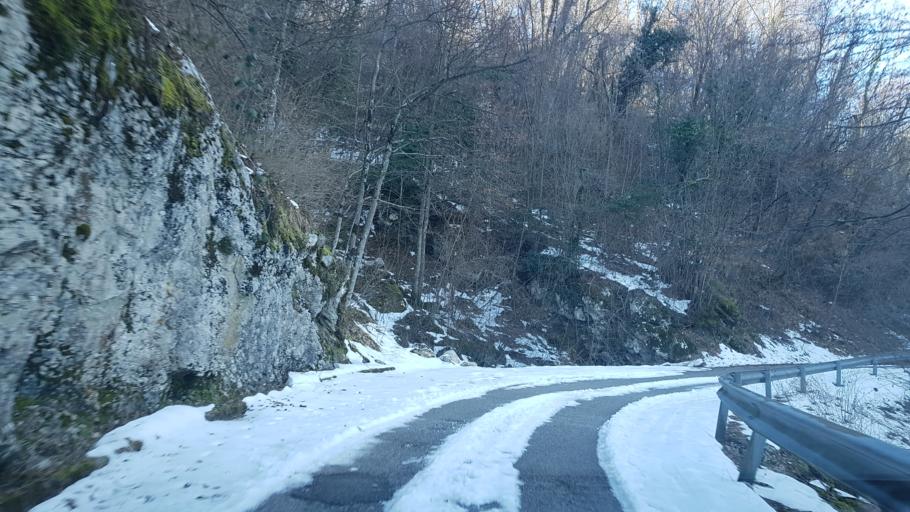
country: IT
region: Friuli Venezia Giulia
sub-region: Provincia di Udine
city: Trasaghis
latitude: 46.2909
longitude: 13.0311
